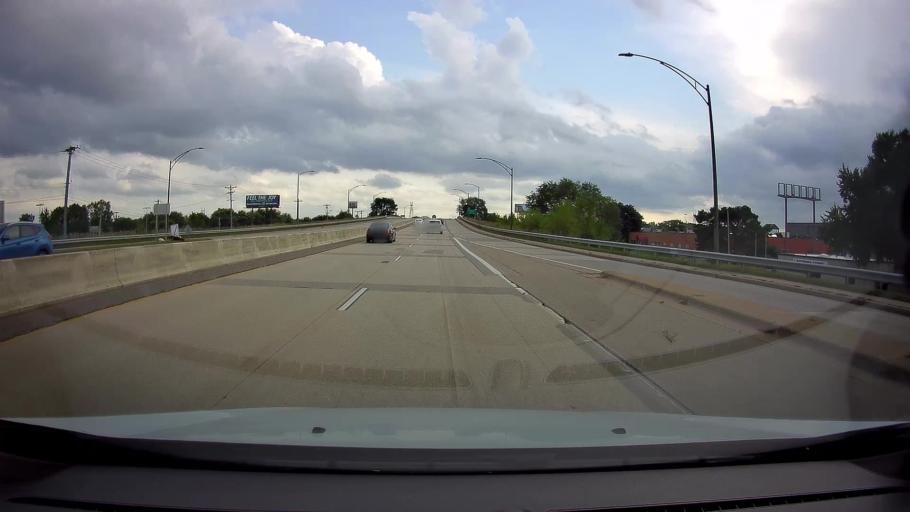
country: US
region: Minnesota
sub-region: Ramsey County
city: Falcon Heights
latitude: 44.9756
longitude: -93.1670
